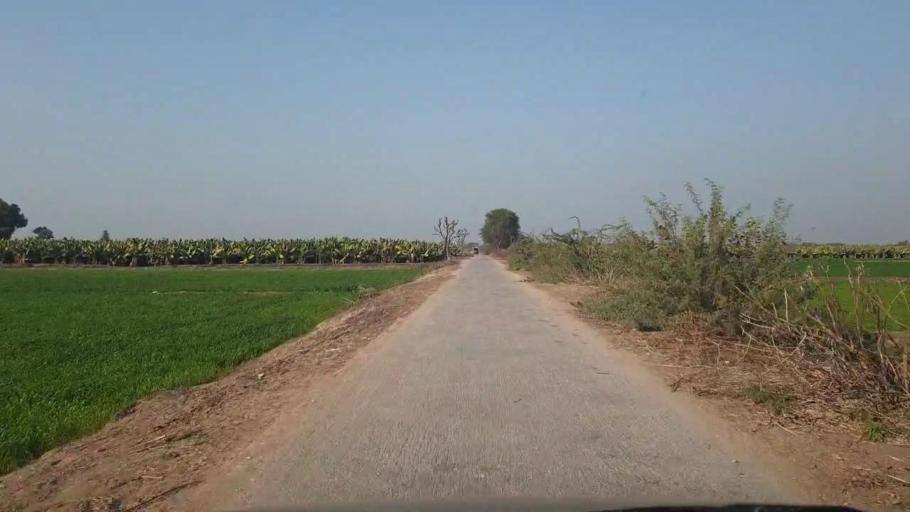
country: PK
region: Sindh
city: Bhit Shah
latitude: 25.8165
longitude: 68.5139
